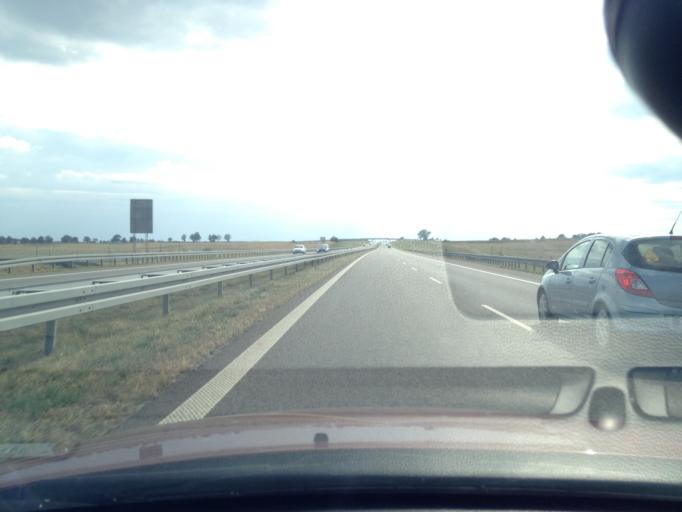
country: PL
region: West Pomeranian Voivodeship
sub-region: Powiat pyrzycki
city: Kozielice
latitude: 53.0422
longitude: 14.8657
